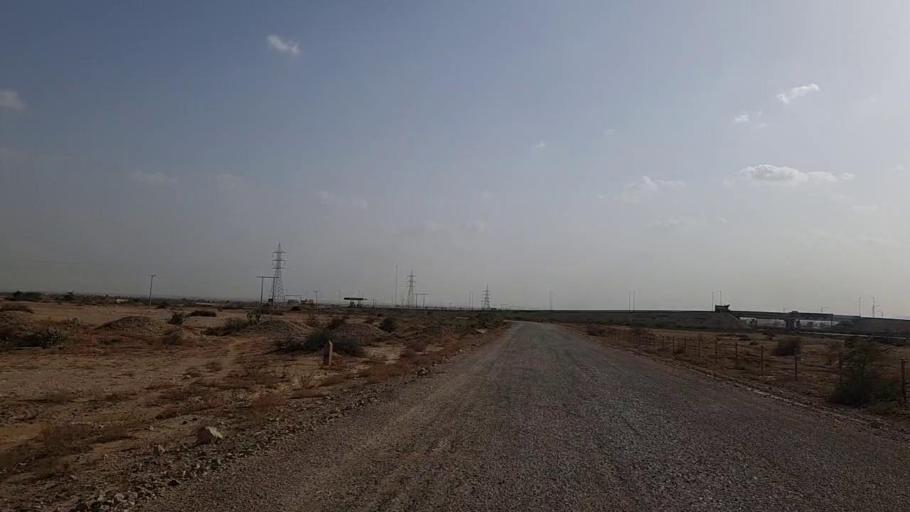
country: PK
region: Sindh
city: Kotri
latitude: 25.2499
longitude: 67.9577
